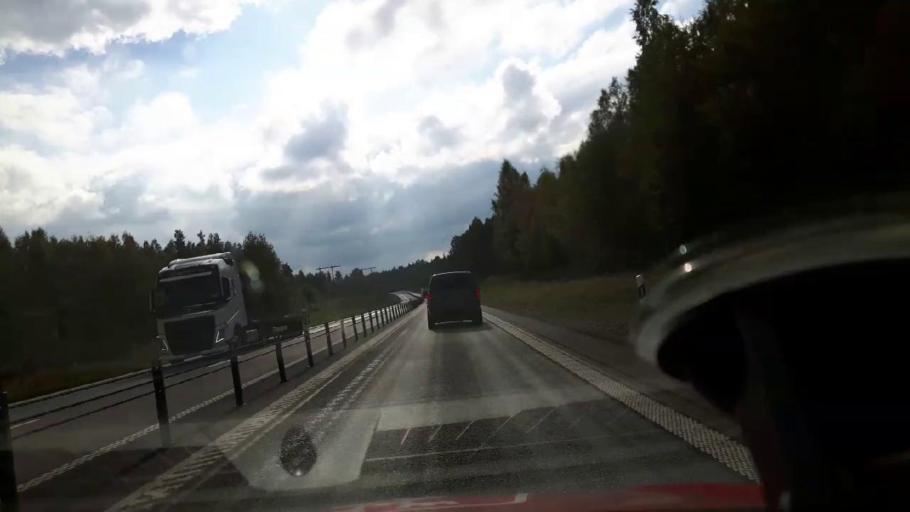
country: SE
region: Gaevleborg
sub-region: Gavle Kommun
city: Norrsundet
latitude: 60.9363
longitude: 17.0145
